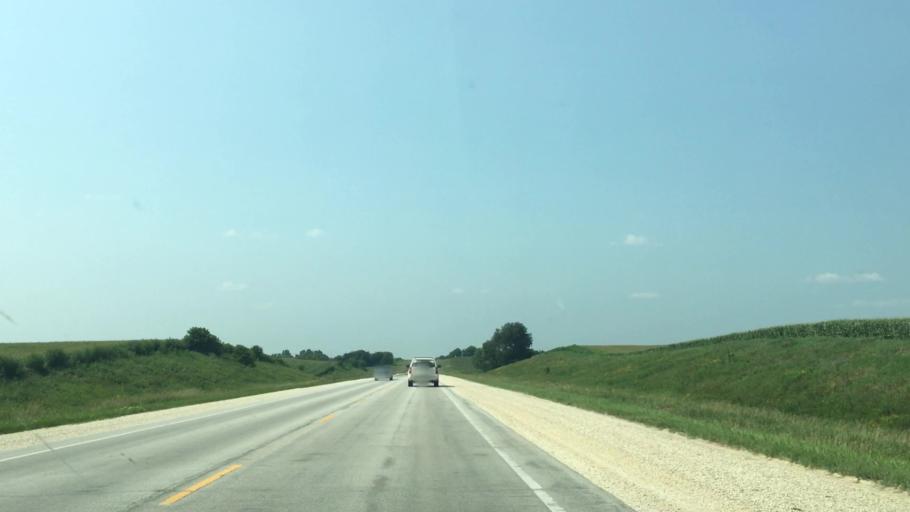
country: US
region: Iowa
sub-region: Winneshiek County
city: Decorah
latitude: 43.3736
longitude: -91.8127
